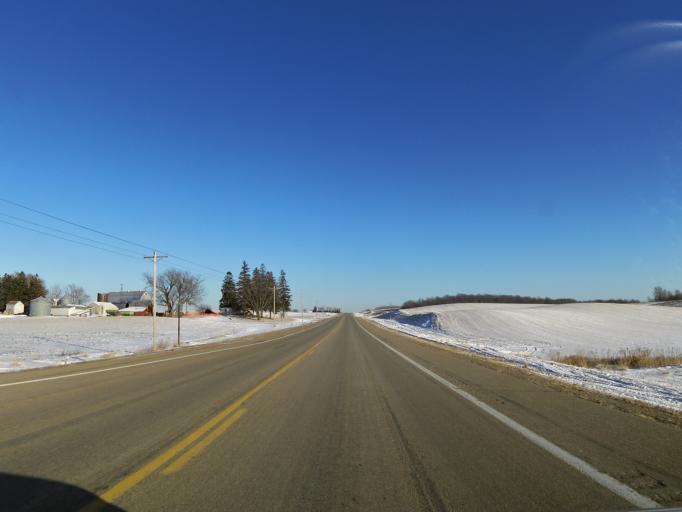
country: US
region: Minnesota
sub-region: Rice County
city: Lonsdale
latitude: 44.4863
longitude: -93.4620
